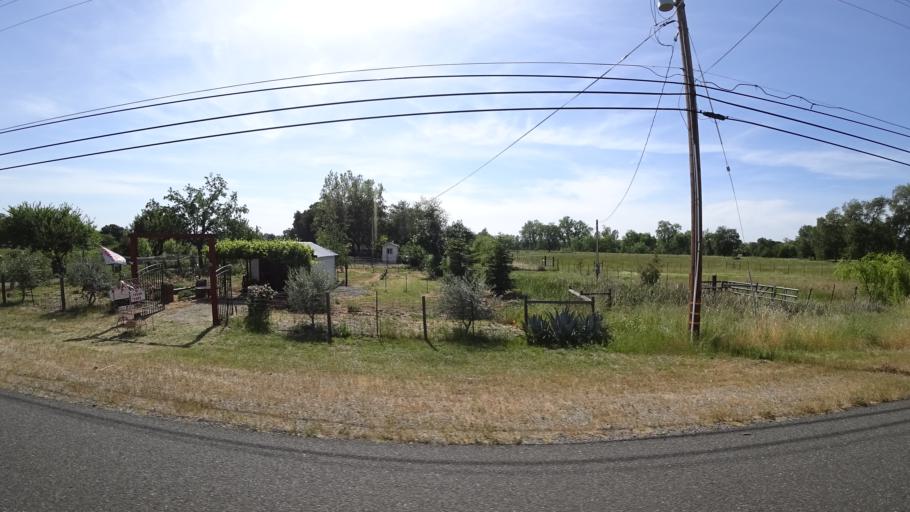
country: US
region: California
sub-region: Tehama County
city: Los Molinos
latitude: 40.0405
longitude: -122.1000
